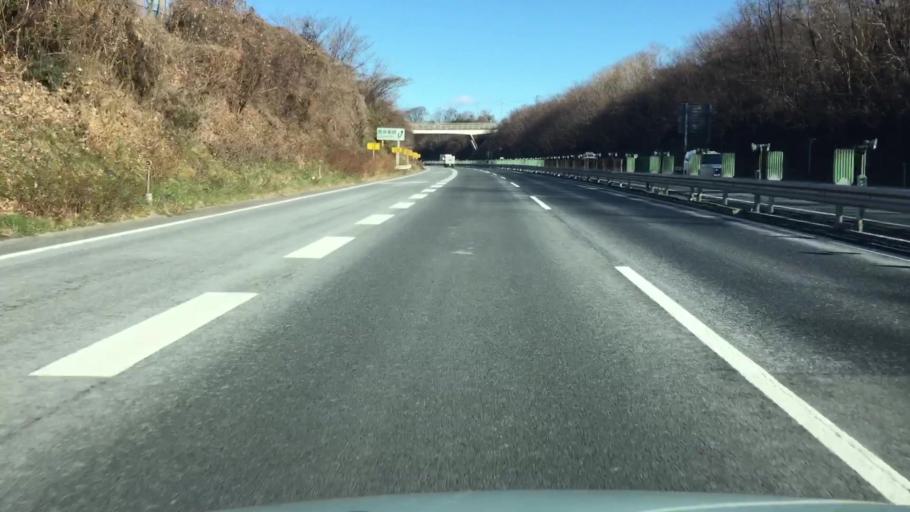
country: JP
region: Gunma
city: Shibukawa
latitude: 36.5427
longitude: 139.0509
